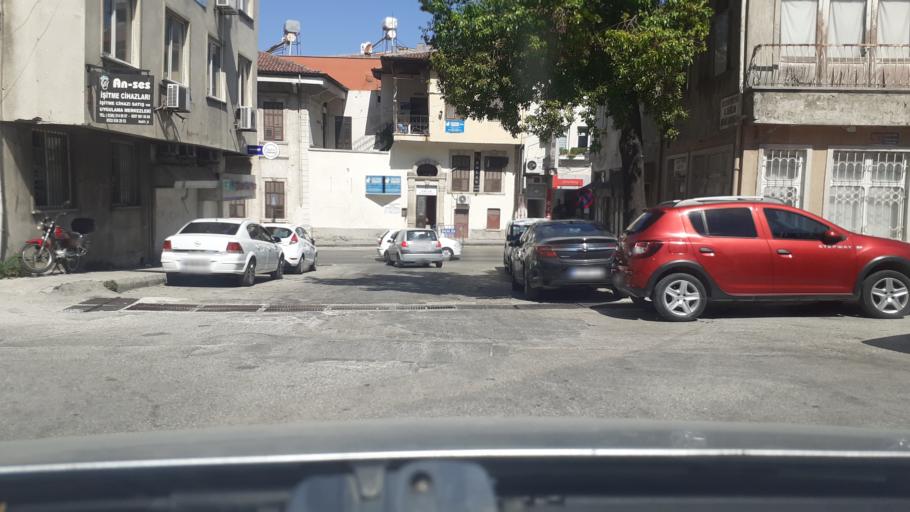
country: TR
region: Hatay
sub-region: Antakya Ilcesi
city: Antakya
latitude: 36.1971
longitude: 36.1618
